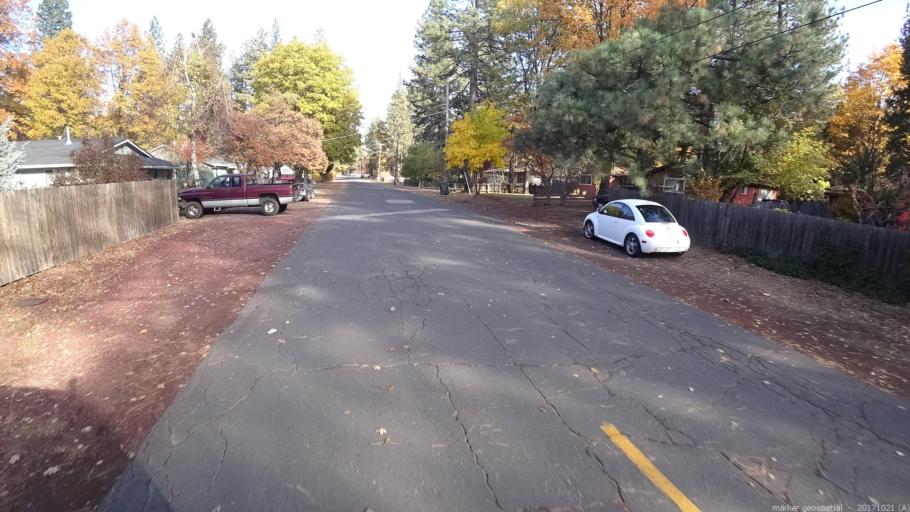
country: US
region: California
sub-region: Shasta County
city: Burney
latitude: 40.8786
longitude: -121.6613
